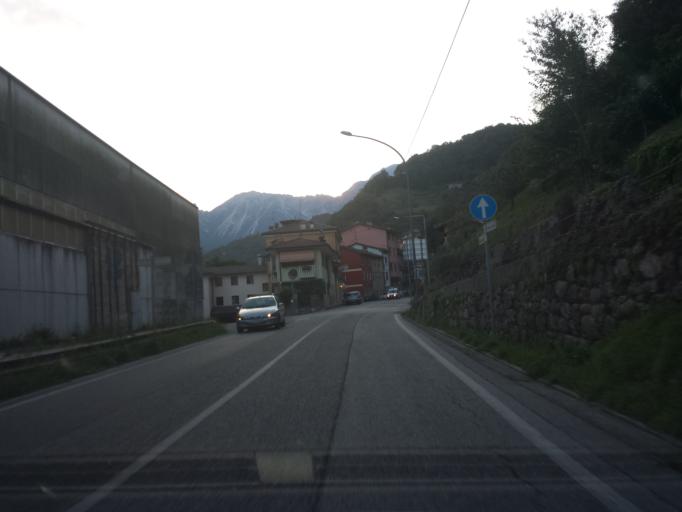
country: IT
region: Veneto
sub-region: Provincia di Vicenza
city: Recoaro Terme
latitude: 45.7062
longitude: 11.2382
